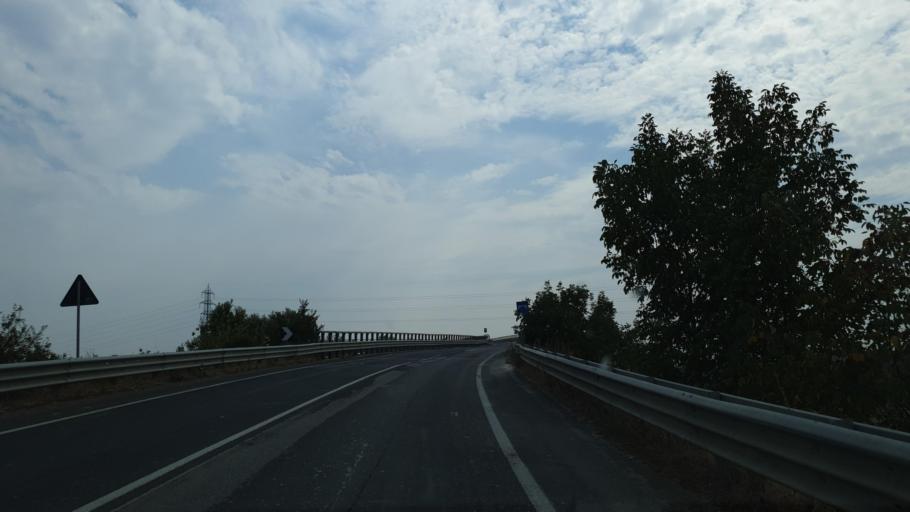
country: IT
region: Emilia-Romagna
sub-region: Provincia di Parma
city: Baganzola
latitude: 44.8637
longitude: 10.2541
